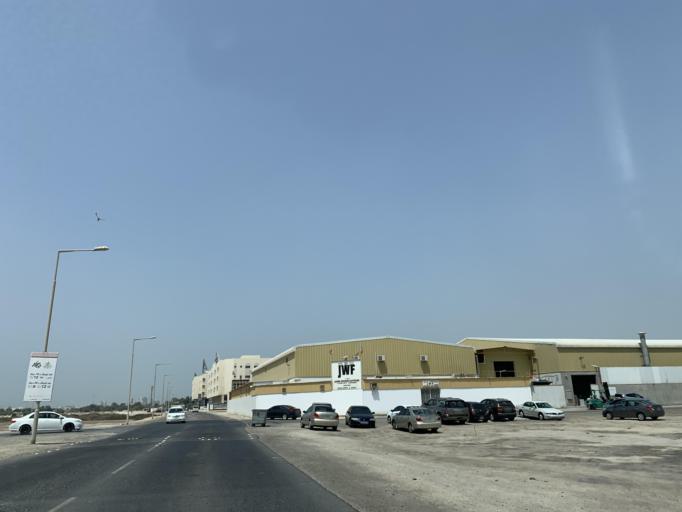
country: BH
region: Northern
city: Madinat `Isa
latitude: 26.1916
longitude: 50.5440
